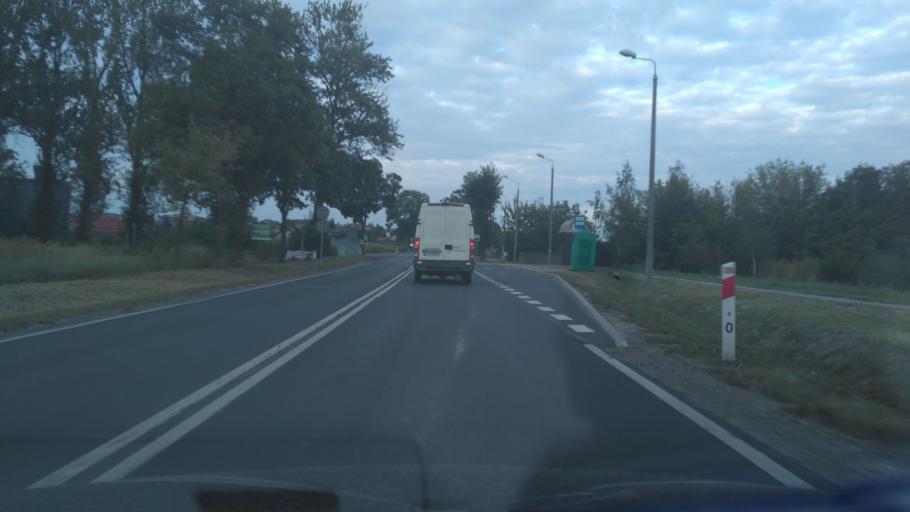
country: PL
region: Lublin Voivodeship
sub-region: Powiat lubelski
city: Jakubowice Murowane
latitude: 51.2824
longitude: 22.6682
